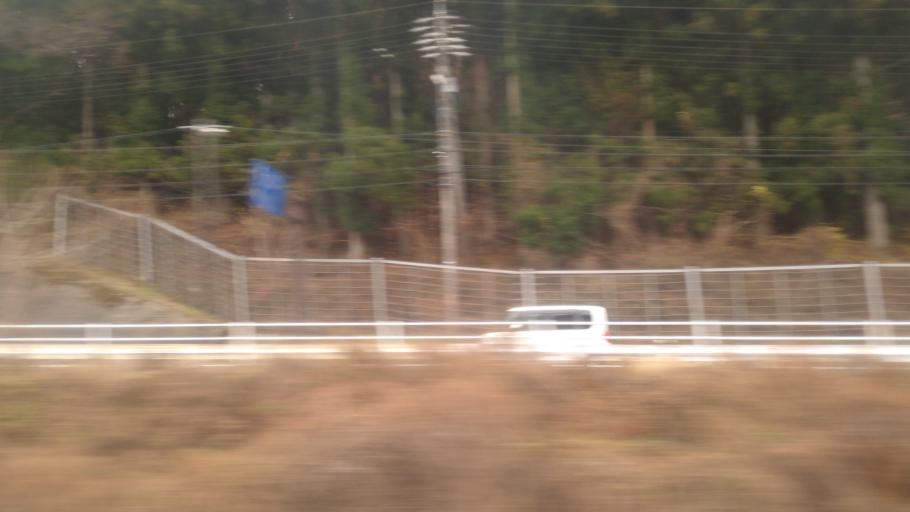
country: JP
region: Nagano
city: Shiojiri
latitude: 36.0571
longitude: 137.9003
